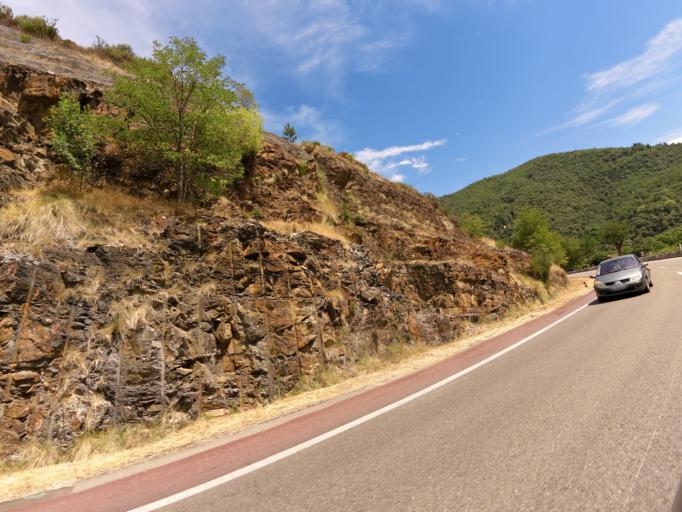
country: FR
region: Languedoc-Roussillon
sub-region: Departement du Gard
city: Sumene
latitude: 43.9821
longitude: 3.6862
